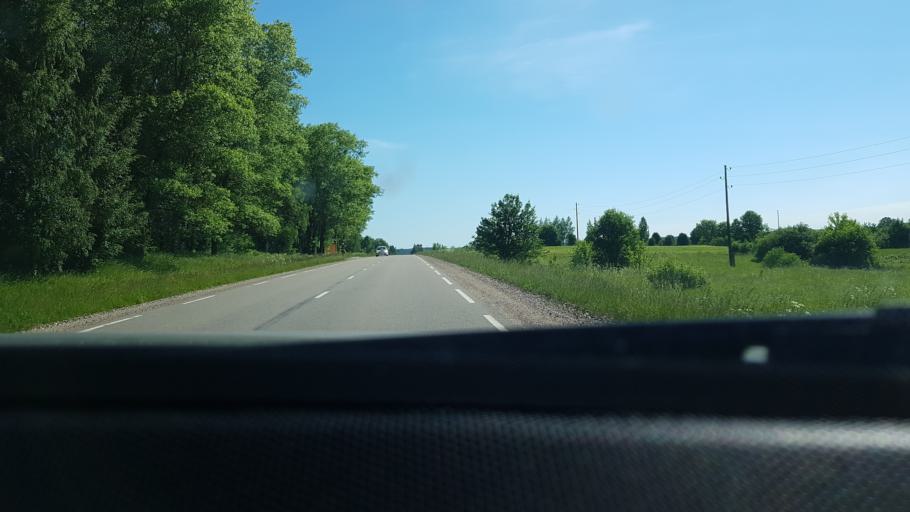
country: BY
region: Vitebsk
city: Braslaw
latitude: 55.8231
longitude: 26.8782
